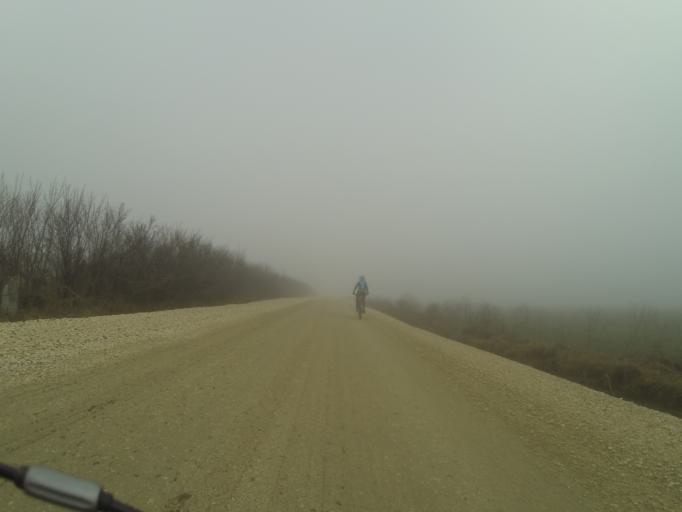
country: RO
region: Mehedinti
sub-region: Comuna Balacita
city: Gvardinita
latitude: 44.4357
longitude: 23.1347
